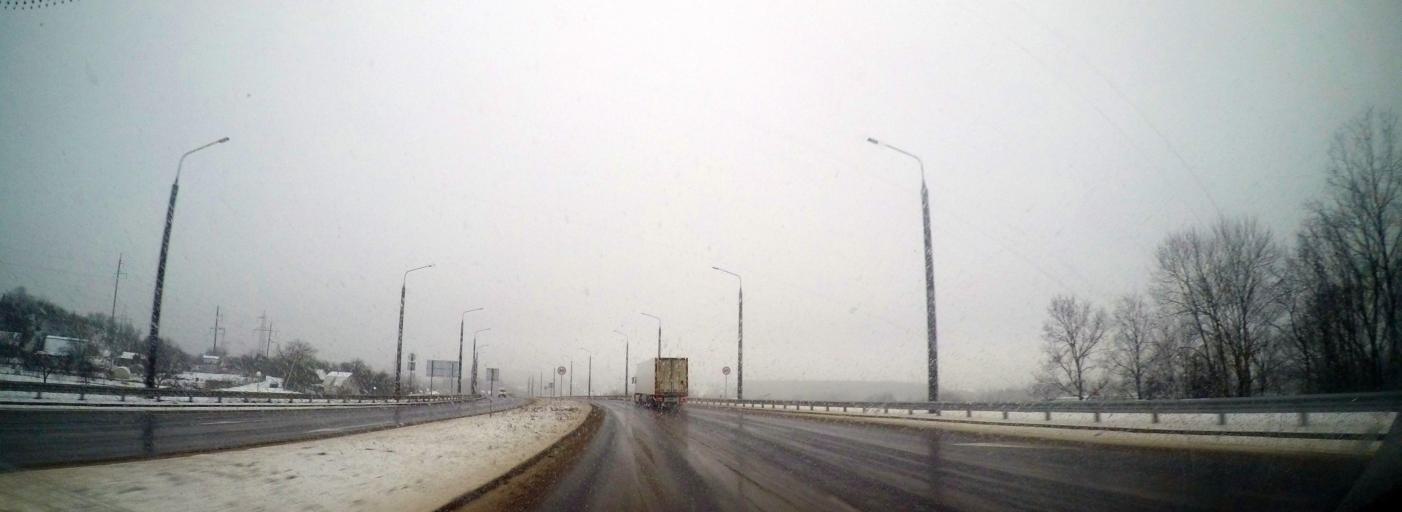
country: BY
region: Grodnenskaya
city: Hrodna
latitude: 53.6630
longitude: 23.8862
